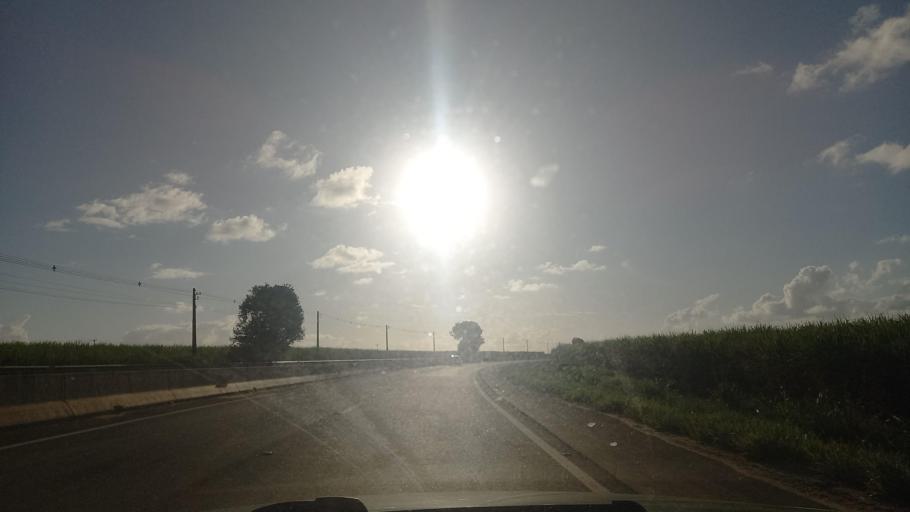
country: BR
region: Alagoas
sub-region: Campo Alegre
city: Campo Alegre
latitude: -9.8230
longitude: -36.2421
